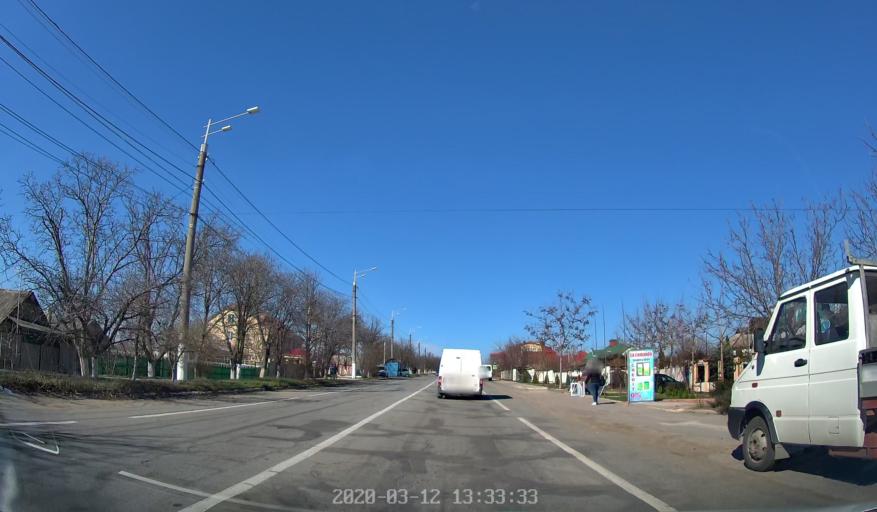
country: MD
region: Laloveni
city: Ialoveni
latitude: 46.9575
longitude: 28.7688
